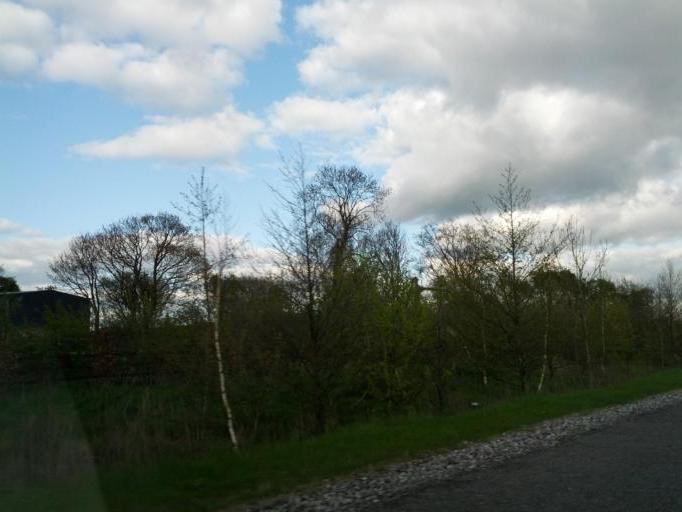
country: IE
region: Leinster
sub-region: An Iarmhi
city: Kilbeggan
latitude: 53.3612
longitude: -7.5165
